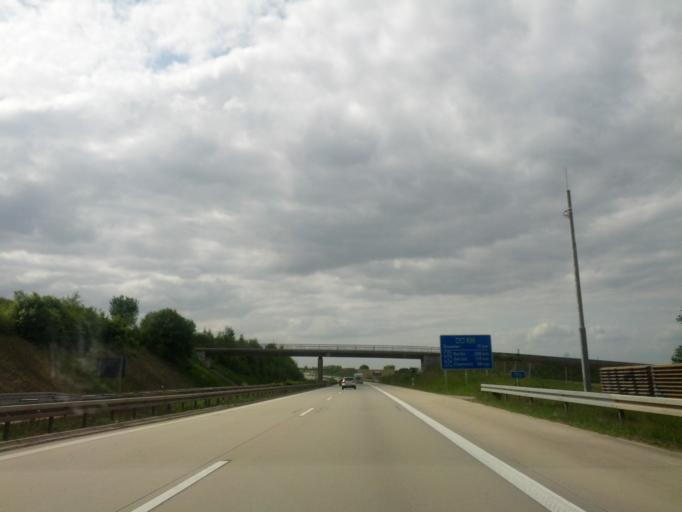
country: DE
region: Saxony
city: Kreischa
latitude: 50.9820
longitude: 13.7891
